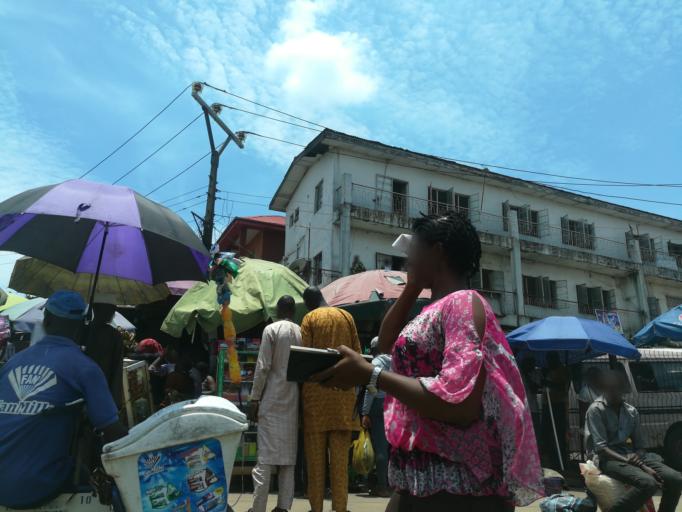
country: NG
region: Lagos
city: Ikorodu
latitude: 6.6204
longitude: 3.5033
